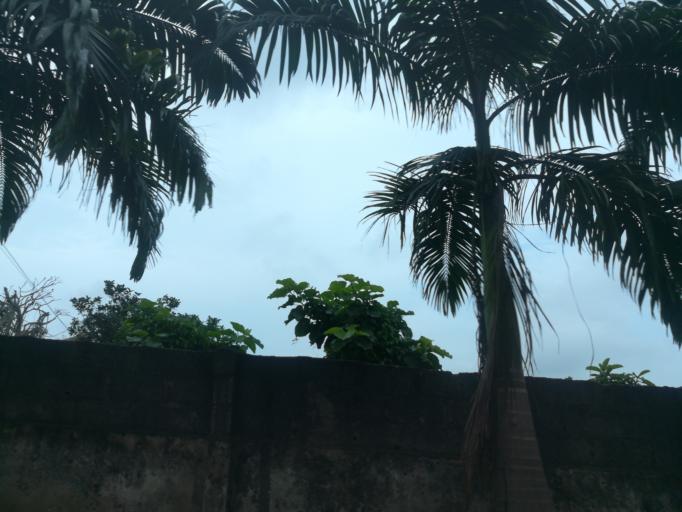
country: NG
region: Lagos
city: Oshodi
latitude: 6.5708
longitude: 3.3565
